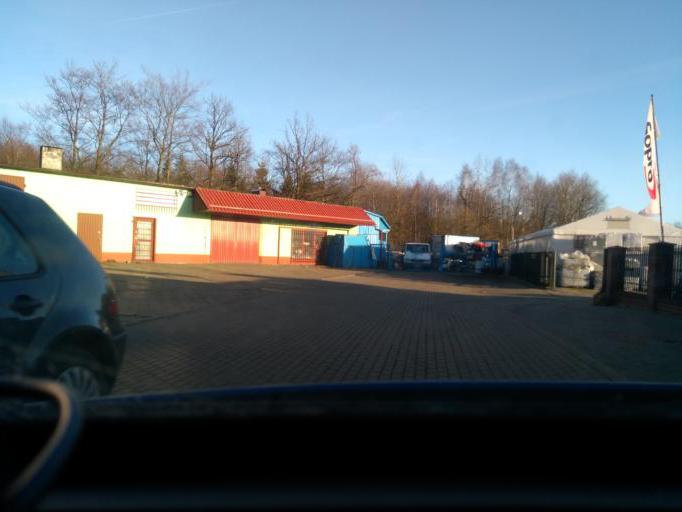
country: PL
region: Pomeranian Voivodeship
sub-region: Powiat kartuski
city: Kartuzy
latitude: 54.3286
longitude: 18.2070
